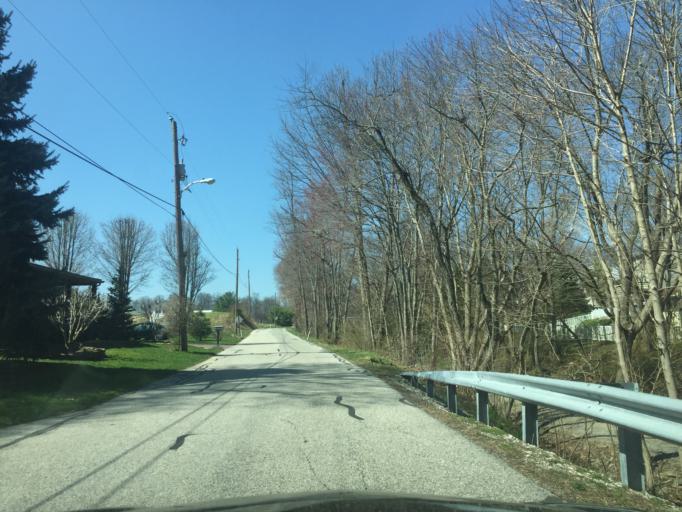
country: US
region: Pennsylvania
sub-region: York County
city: New Freedom
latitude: 39.7258
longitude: -76.7010
